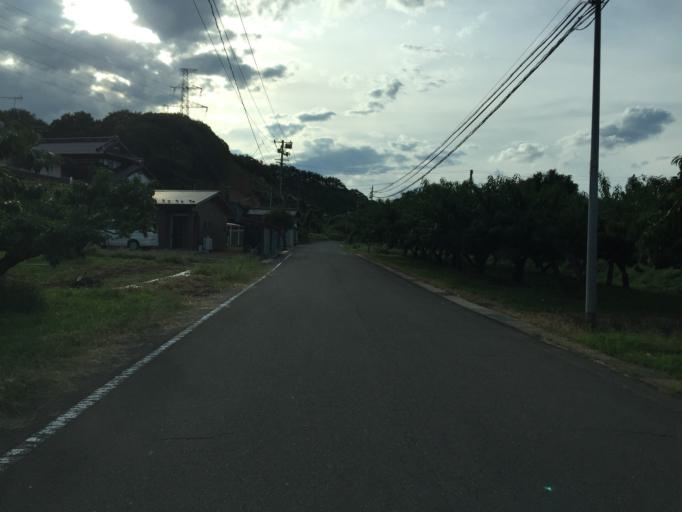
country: JP
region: Fukushima
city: Hobaramachi
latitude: 37.8031
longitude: 140.5170
